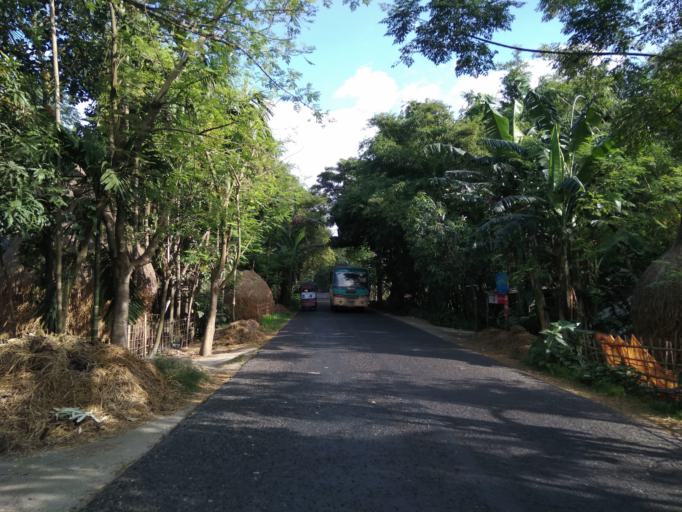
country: BD
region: Rangpur Division
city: Rangpur
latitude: 25.8401
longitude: 89.1137
